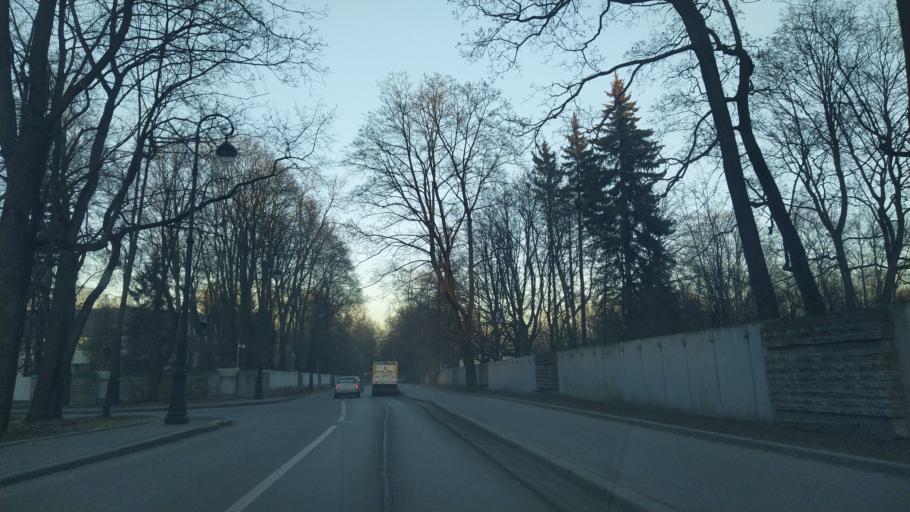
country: RU
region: St.-Petersburg
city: Novaya Derevnya
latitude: 59.9751
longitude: 30.2883
